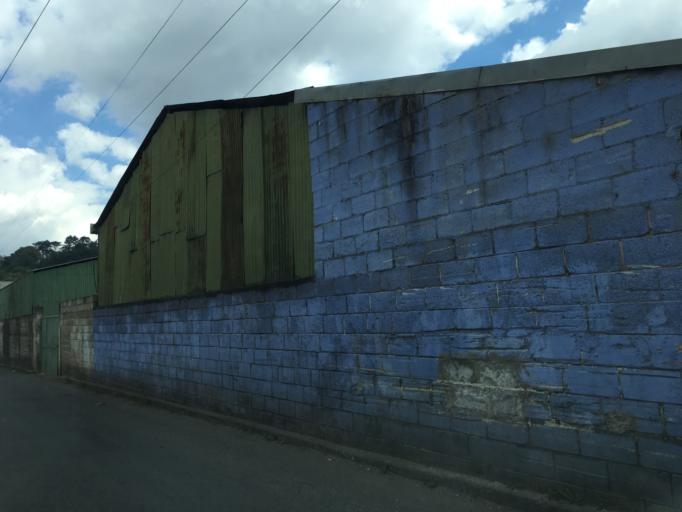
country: GT
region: Guatemala
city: San Jose Pinula
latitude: 14.5732
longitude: -90.4453
